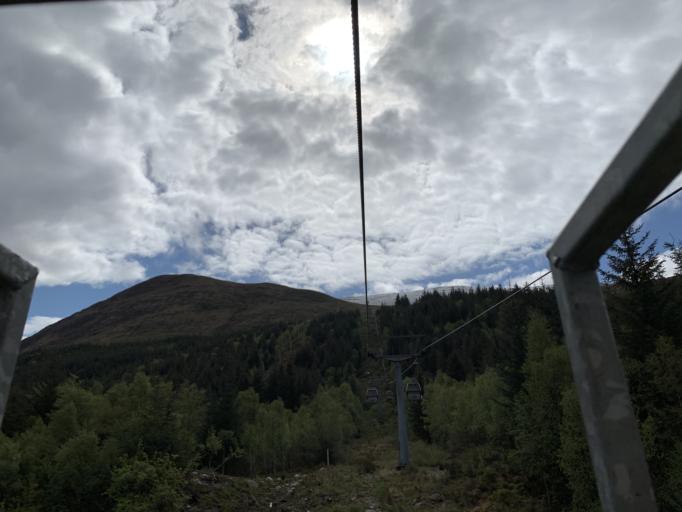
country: GB
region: Scotland
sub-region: Highland
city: Spean Bridge
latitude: 56.8468
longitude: -4.9897
